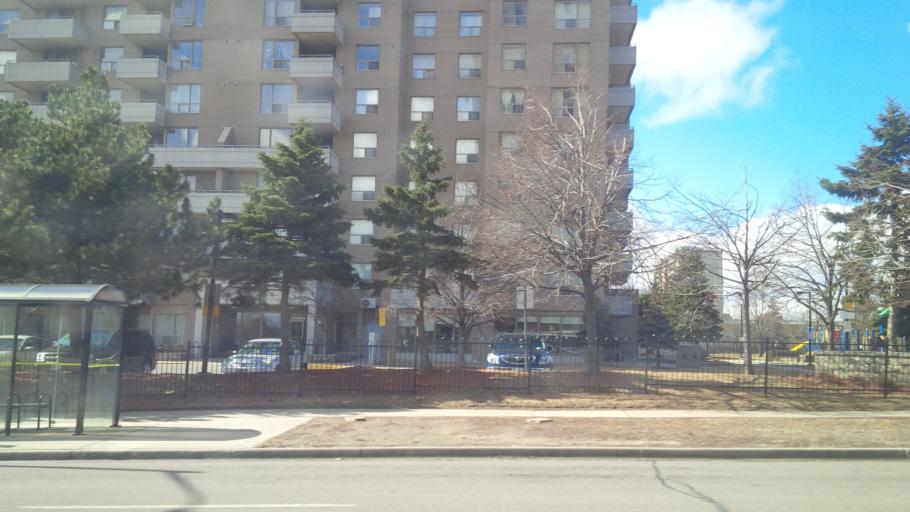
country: CA
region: Ontario
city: Brampton
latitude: 43.7189
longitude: -79.7165
